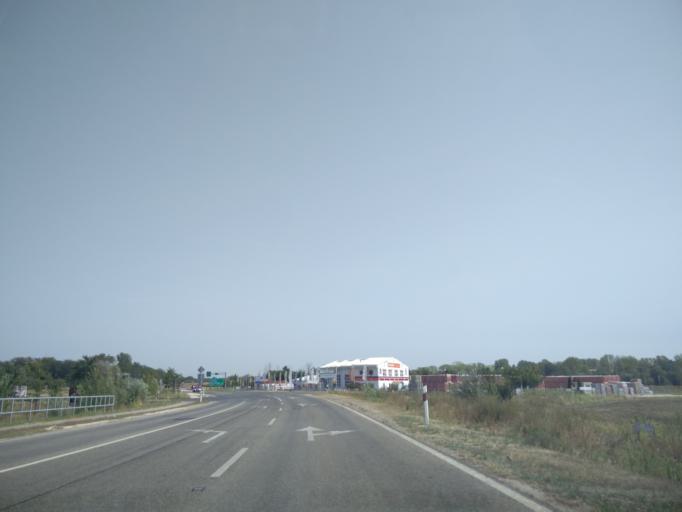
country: HU
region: Csongrad
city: Szeged
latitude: 46.2809
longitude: 20.0893
